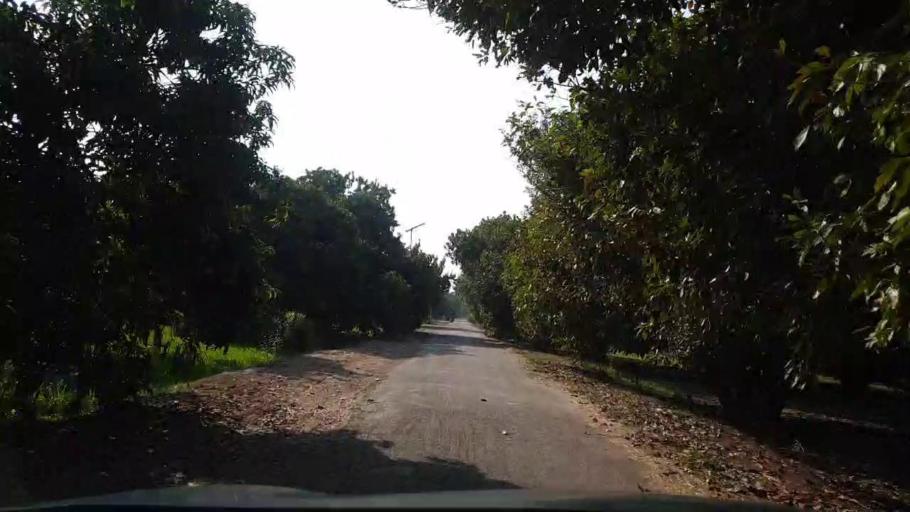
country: PK
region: Sindh
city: Tando Allahyar
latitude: 25.5018
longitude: 68.8620
